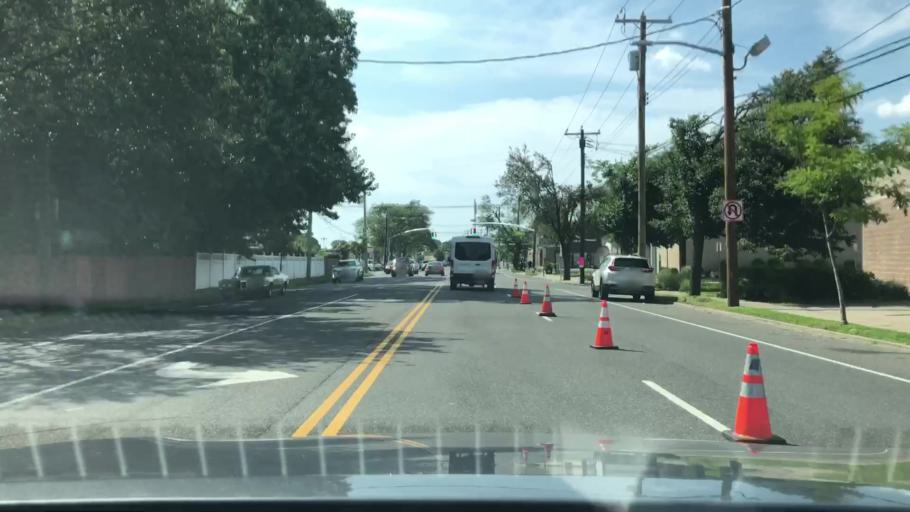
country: US
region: New York
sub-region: Nassau County
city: South Hempstead
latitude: 40.6831
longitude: -73.6153
